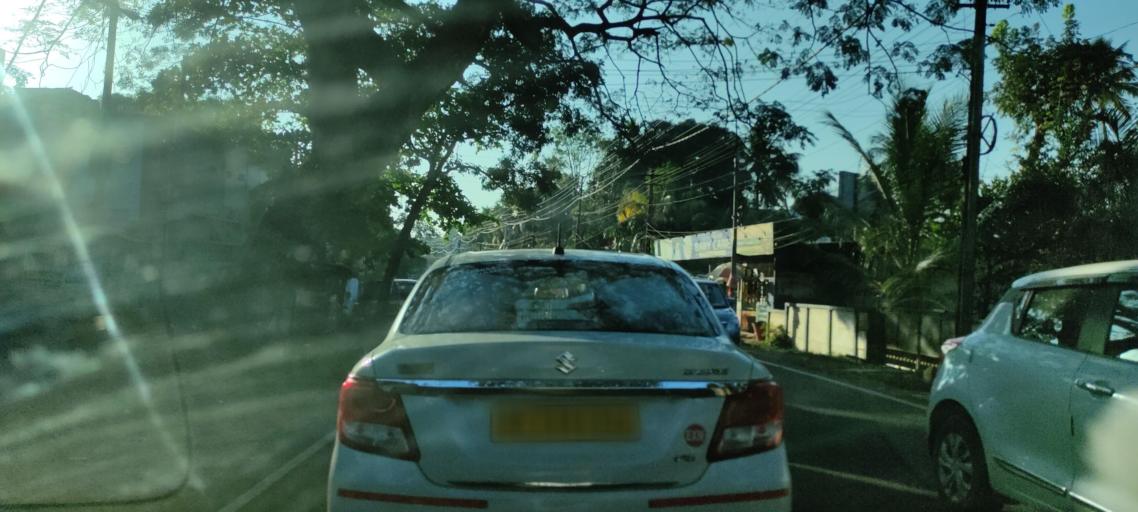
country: IN
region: Kerala
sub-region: Alappuzha
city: Kattanam
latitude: 9.1766
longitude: 76.5694
